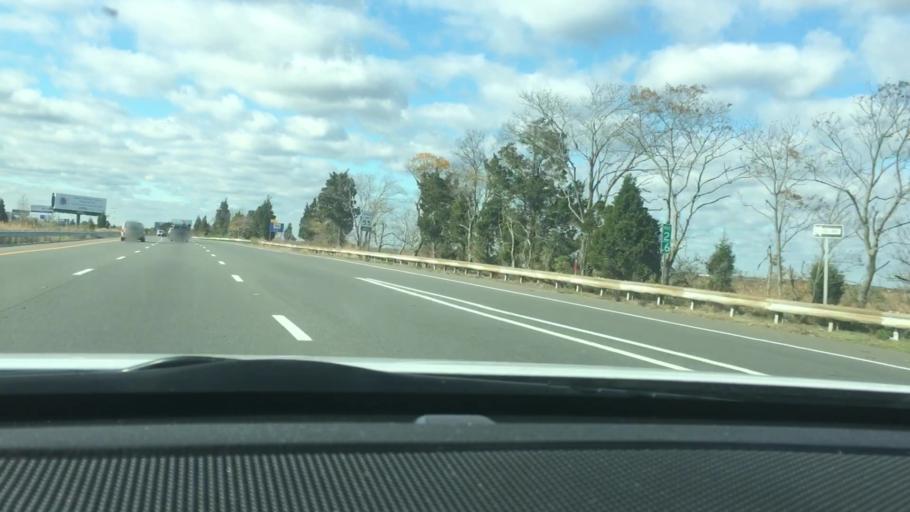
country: US
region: New Jersey
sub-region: Atlantic County
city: Ventnor City
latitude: 39.3781
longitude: -74.4837
